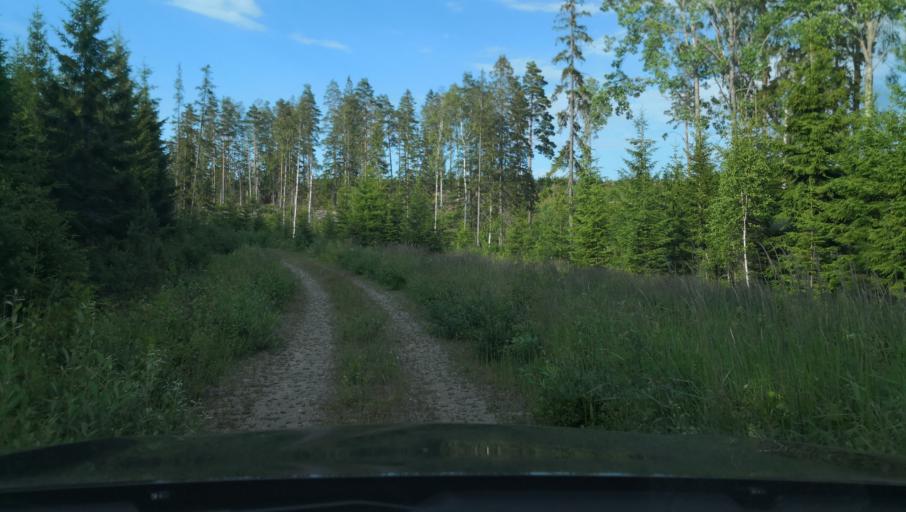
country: SE
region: Dalarna
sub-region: Ludvika Kommun
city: Ludvika
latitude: 60.0767
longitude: 15.2943
